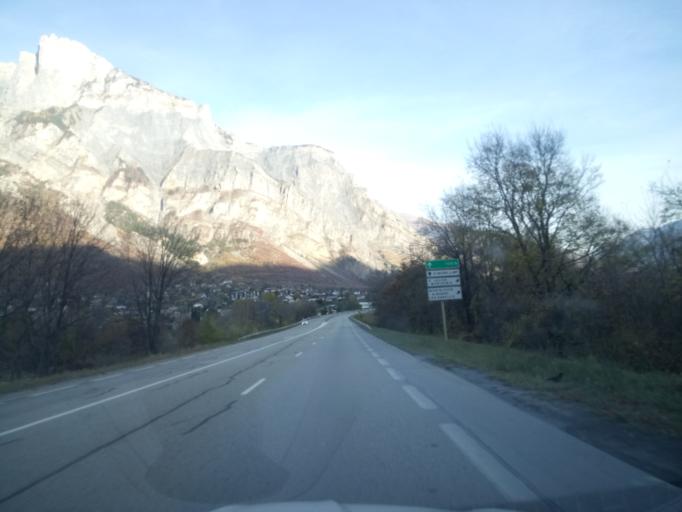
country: FR
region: Rhone-Alpes
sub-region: Departement de la Savoie
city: Villargondran
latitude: 45.2529
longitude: 6.4048
